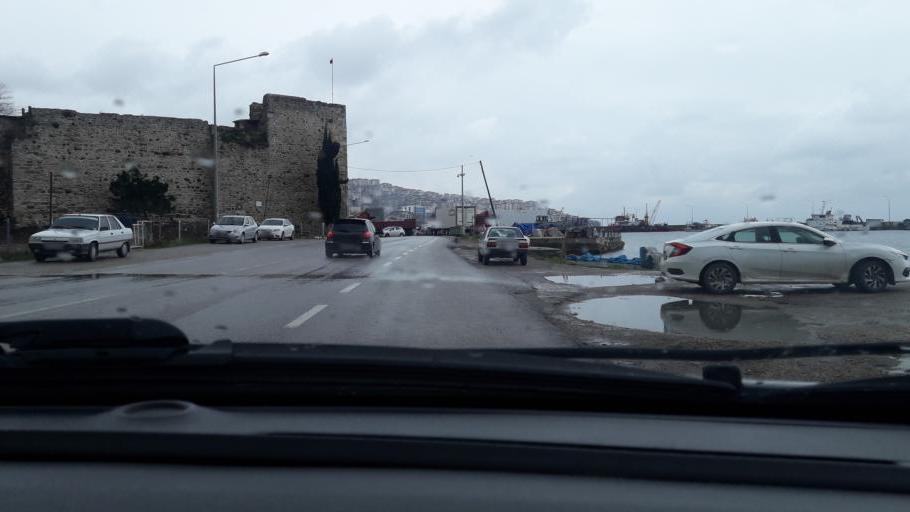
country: TR
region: Sinop
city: Sinop
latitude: 42.0237
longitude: 35.1421
